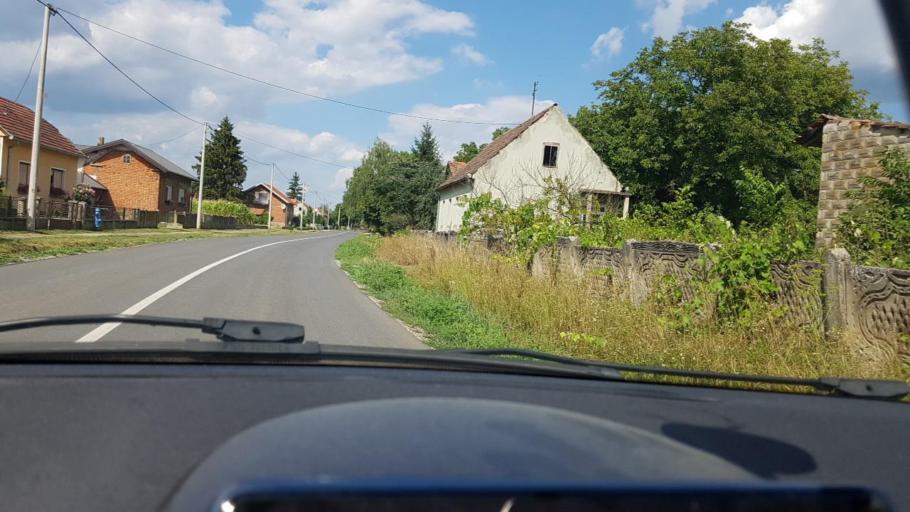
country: HR
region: Bjelovarsko-Bilogorska
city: Zdralovi
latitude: 45.8462
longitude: 16.9735
